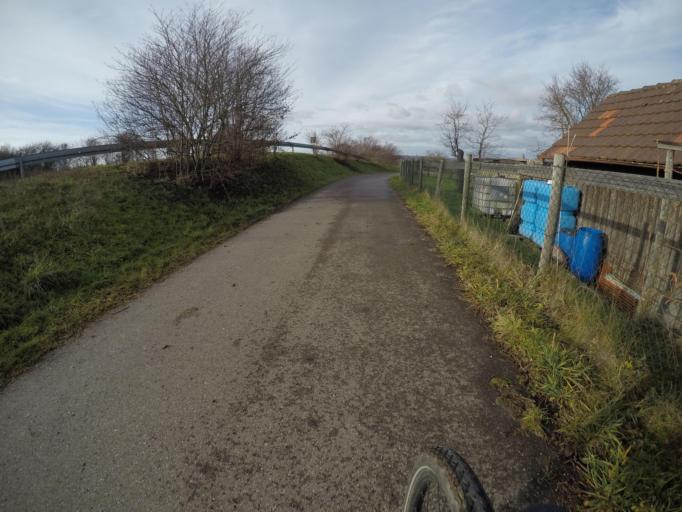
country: DE
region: Baden-Wuerttemberg
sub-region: Regierungsbezirk Stuttgart
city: Oberboihingen
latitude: 48.6291
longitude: 9.3745
